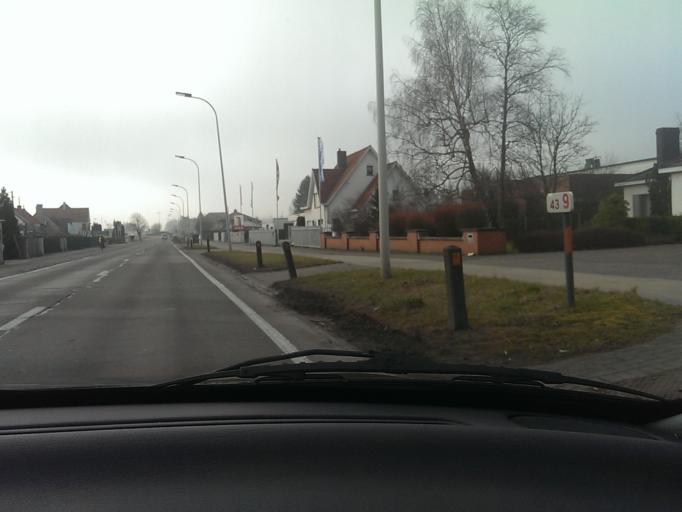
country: BE
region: Flanders
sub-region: Provincie West-Vlaanderen
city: Ledegem
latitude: 50.8453
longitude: 3.1112
